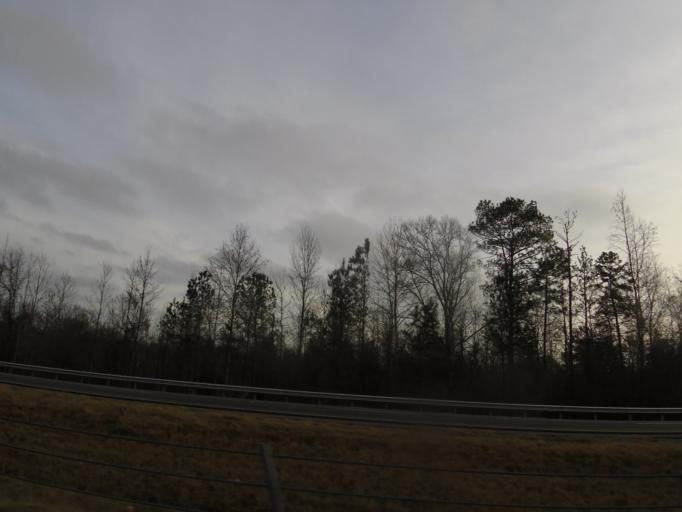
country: US
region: Alabama
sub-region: Autauga County
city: Marbury
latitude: 32.7240
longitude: -86.5346
